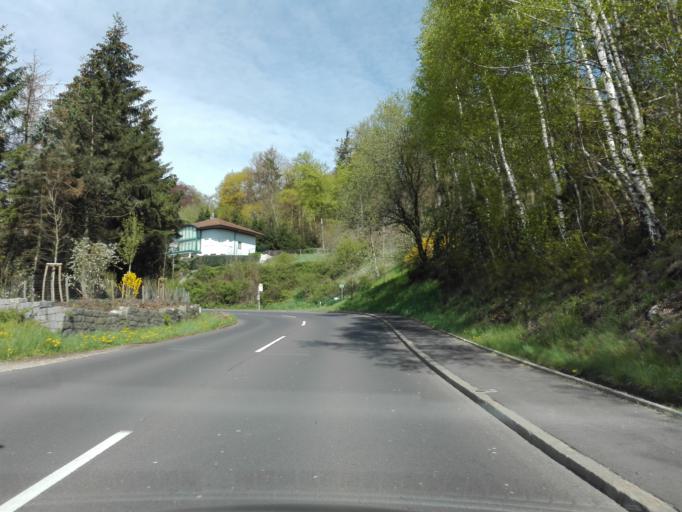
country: AT
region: Upper Austria
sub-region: Linz Stadt
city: Linz
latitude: 48.3171
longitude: 14.2564
